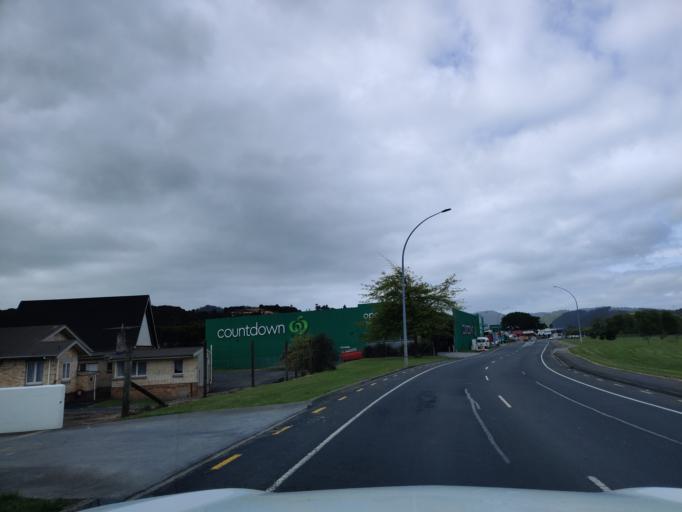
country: NZ
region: Waikato
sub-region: Waikato District
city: Ngaruawahia
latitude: -37.5629
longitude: 175.1585
